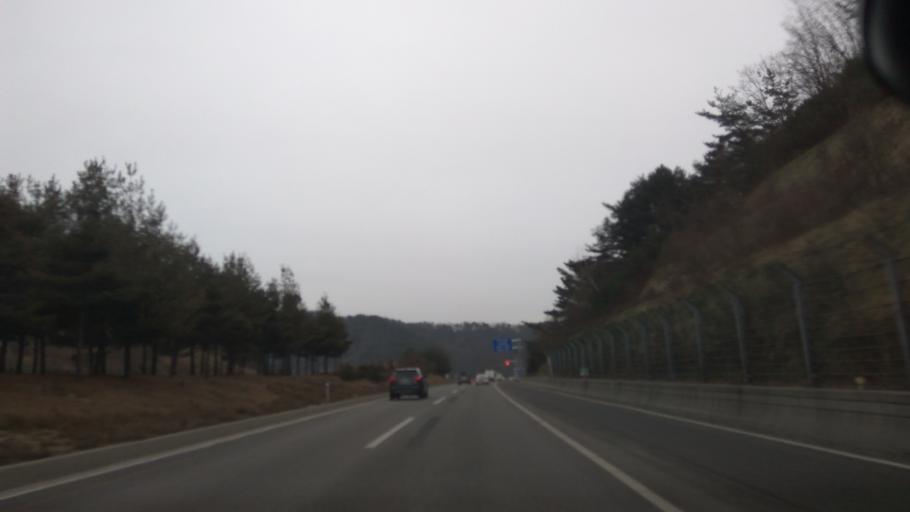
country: KR
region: Gangwon-do
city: Sindong
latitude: 37.7401
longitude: 127.6497
